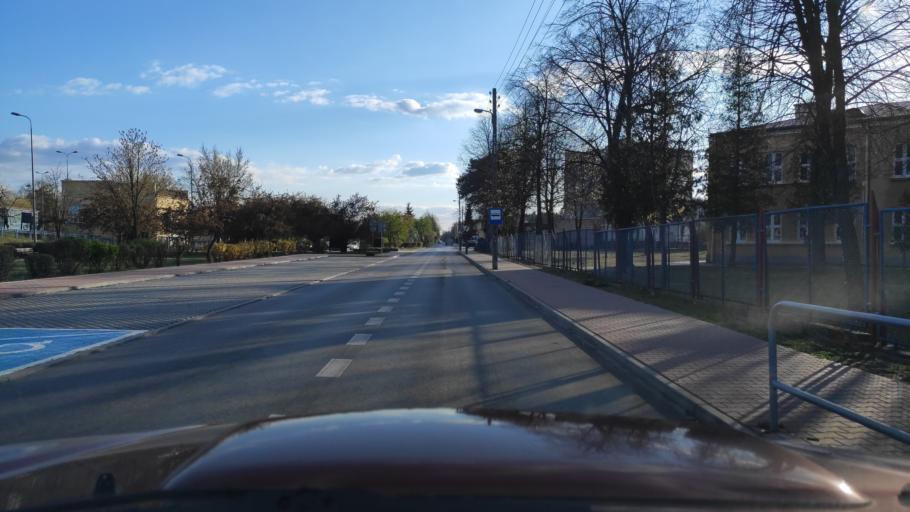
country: PL
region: Masovian Voivodeship
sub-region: Powiat radomski
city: Pionki
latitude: 51.4729
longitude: 21.4418
